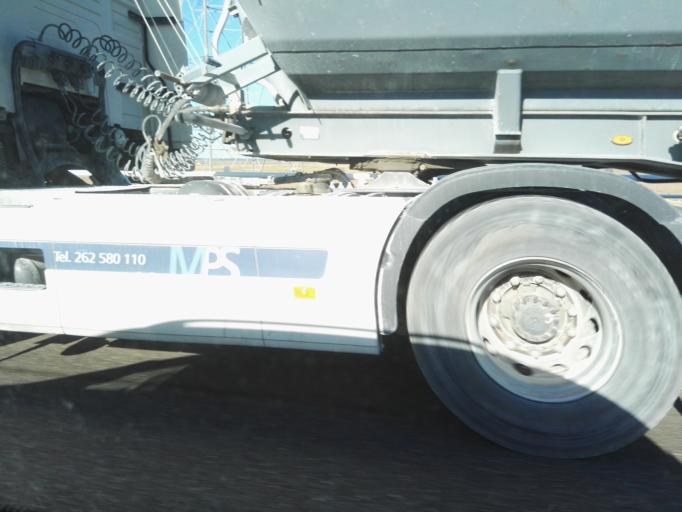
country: PT
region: Santarem
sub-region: Benavente
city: Samora Correia
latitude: 38.9848
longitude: -8.8887
